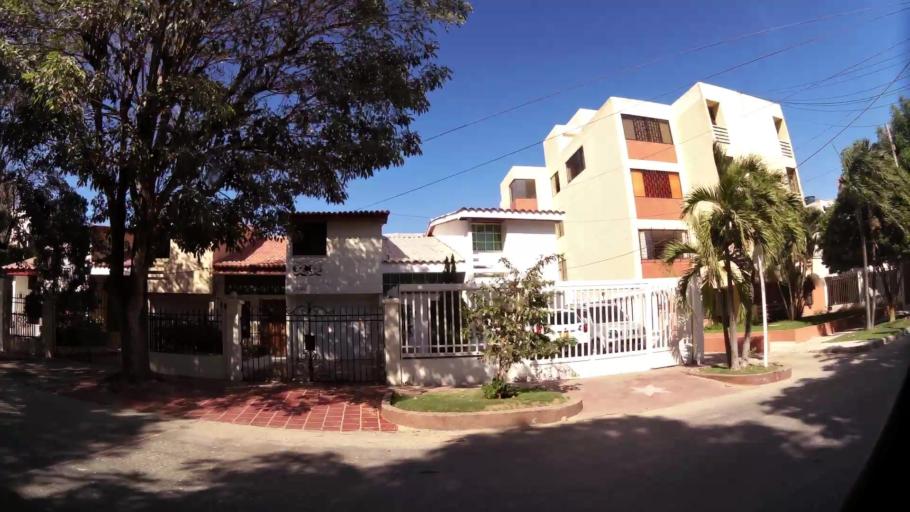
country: CO
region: Atlantico
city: Barranquilla
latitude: 11.0167
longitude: -74.8161
